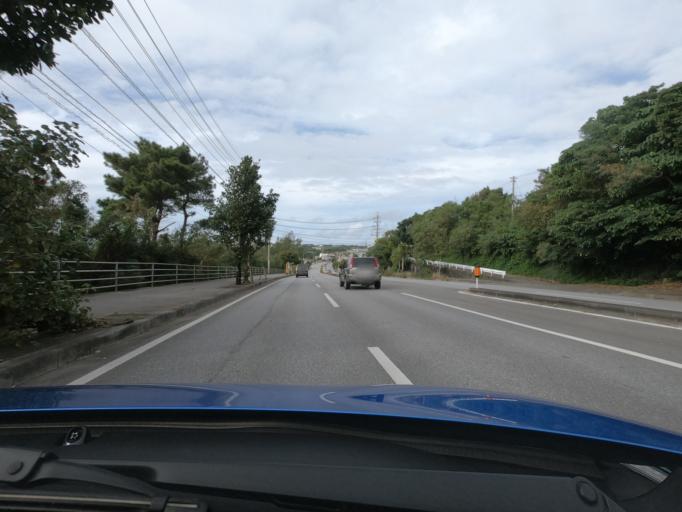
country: JP
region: Okinawa
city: Nago
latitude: 26.6677
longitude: 127.8902
